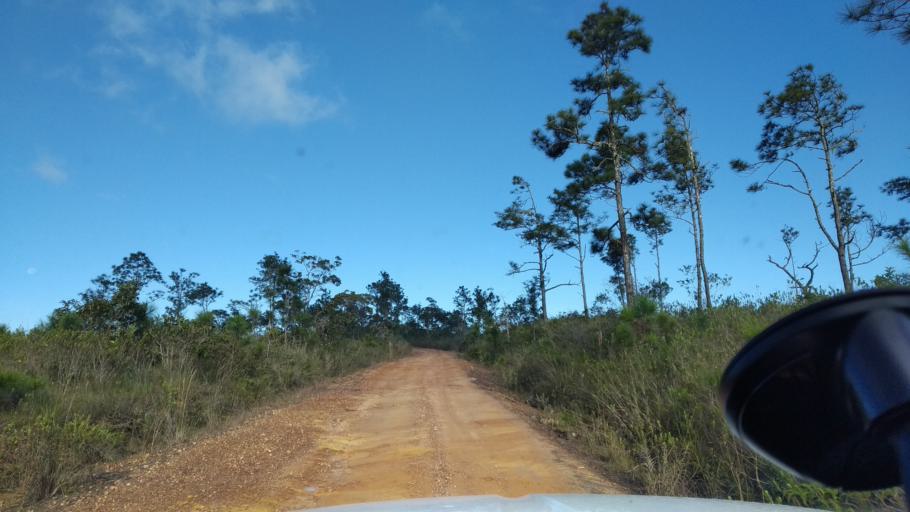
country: BZ
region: Cayo
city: Belmopan
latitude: 16.9962
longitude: -88.8372
